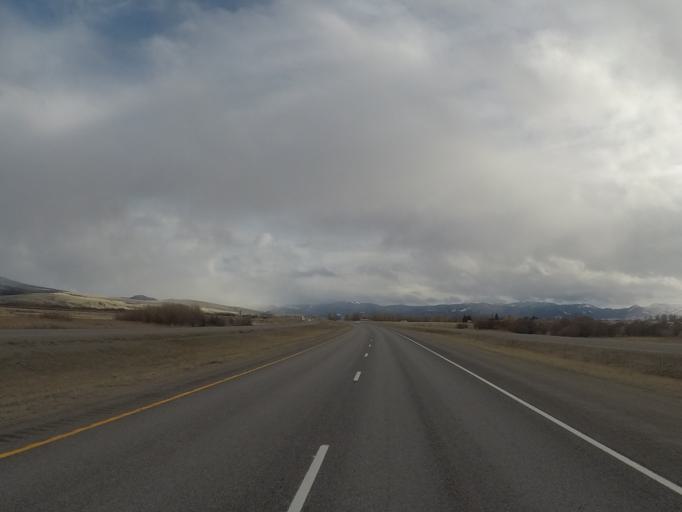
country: US
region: Montana
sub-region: Deer Lodge County
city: Warm Springs
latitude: 46.1935
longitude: -112.7830
